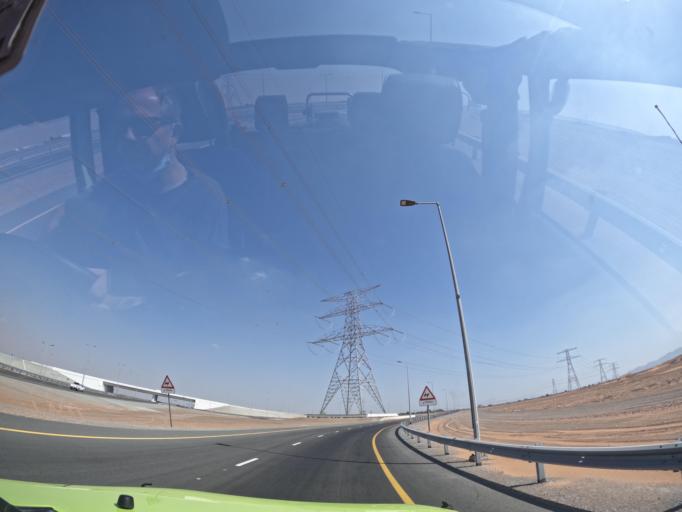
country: AE
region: Ash Shariqah
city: Adh Dhayd
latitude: 24.8115
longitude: 55.8024
